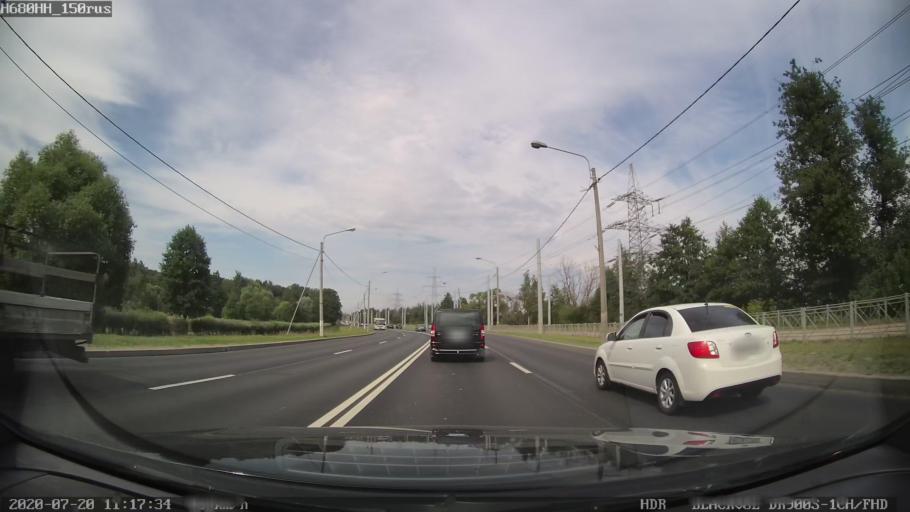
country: RU
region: St.-Petersburg
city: Sosnovaya Polyana
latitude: 59.8518
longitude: 30.1137
